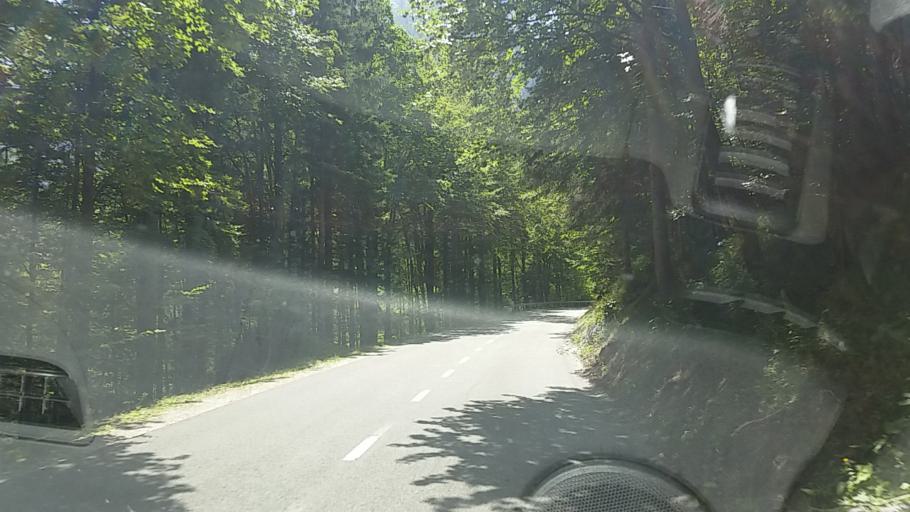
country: SI
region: Kranjska Gora
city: Kranjska Gora
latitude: 46.4490
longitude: 13.7767
